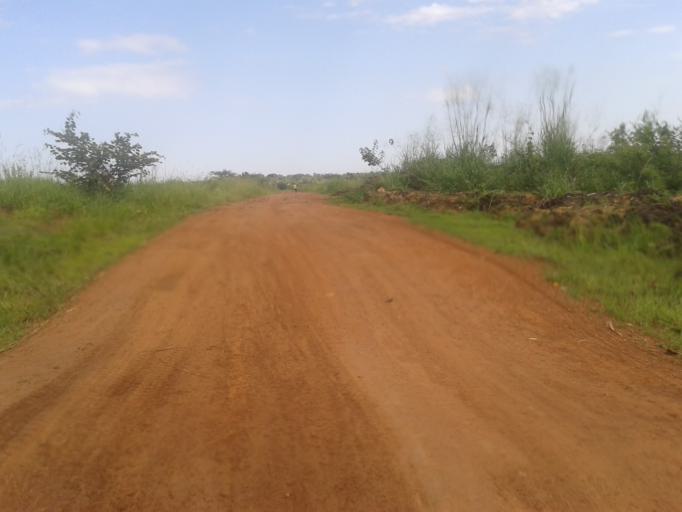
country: UG
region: Northern Region
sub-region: Gulu District
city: Gulu
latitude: 2.8232
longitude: 32.2638
